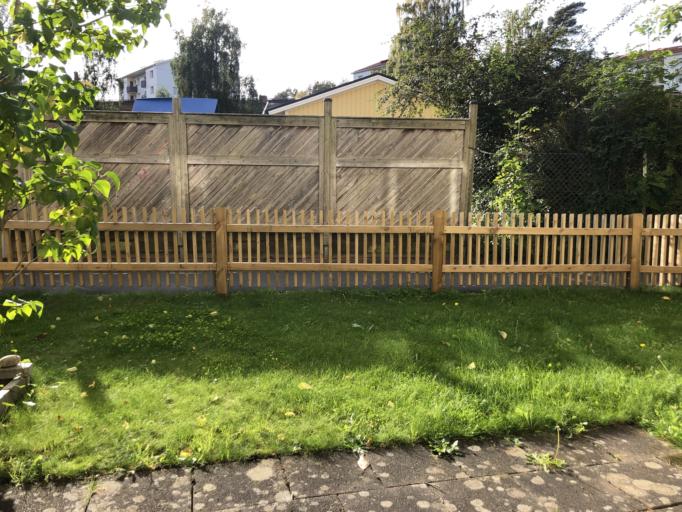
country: SE
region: Vaestra Goetaland
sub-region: Goteborg
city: Eriksbo
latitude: 57.7600
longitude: 12.0354
